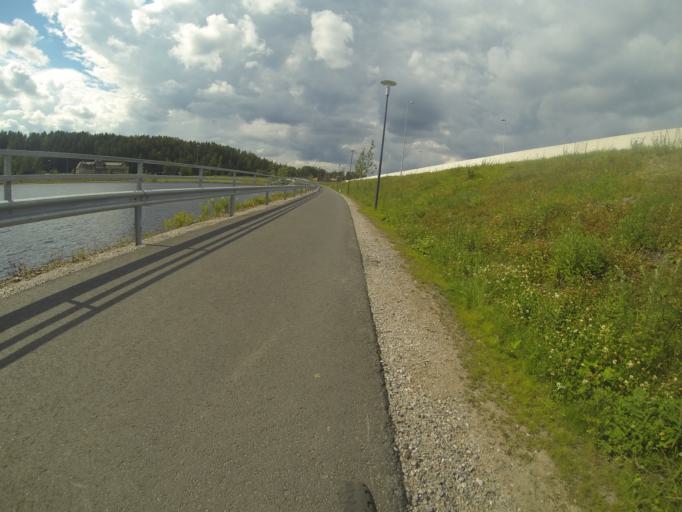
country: FI
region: Southern Savonia
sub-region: Savonlinna
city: Savonlinna
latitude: 61.8750
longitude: 28.8784
